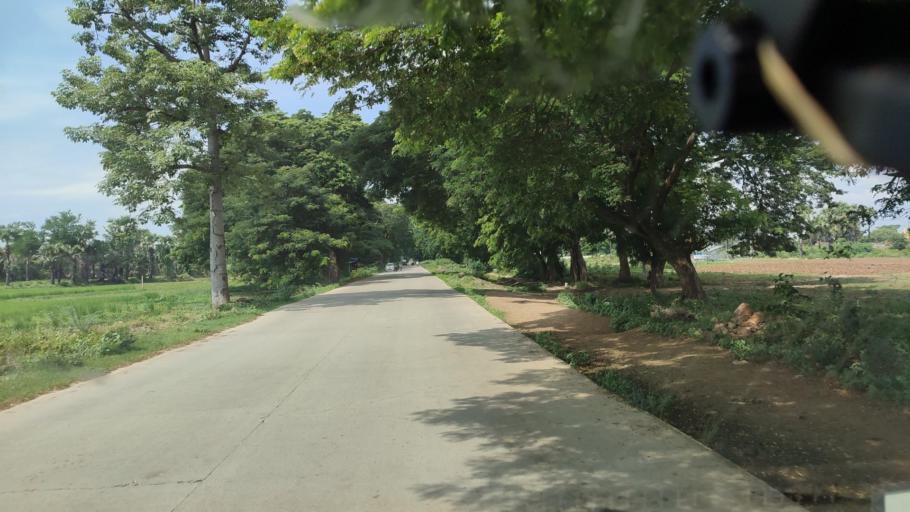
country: MM
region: Magway
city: Pakokku
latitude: 21.3262
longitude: 95.2307
